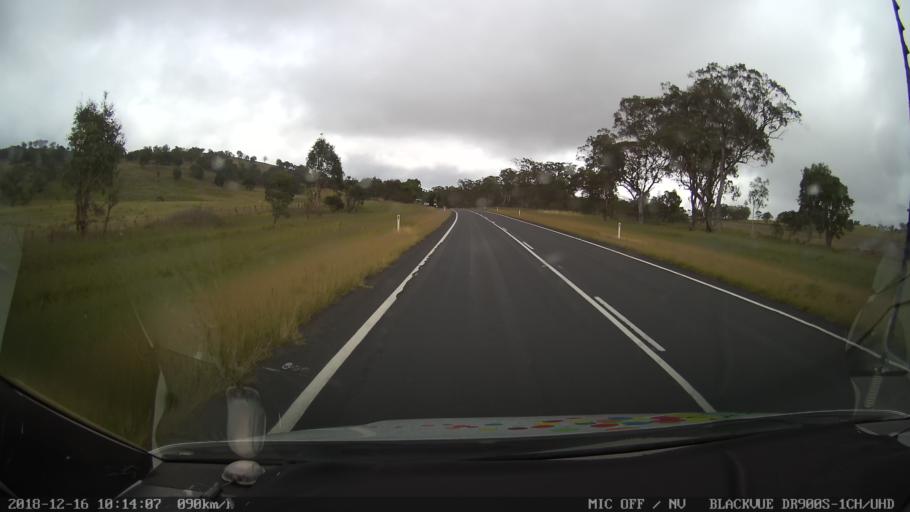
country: AU
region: New South Wales
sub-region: Tenterfield Municipality
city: Carrolls Creek
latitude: -29.2905
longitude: 151.9603
